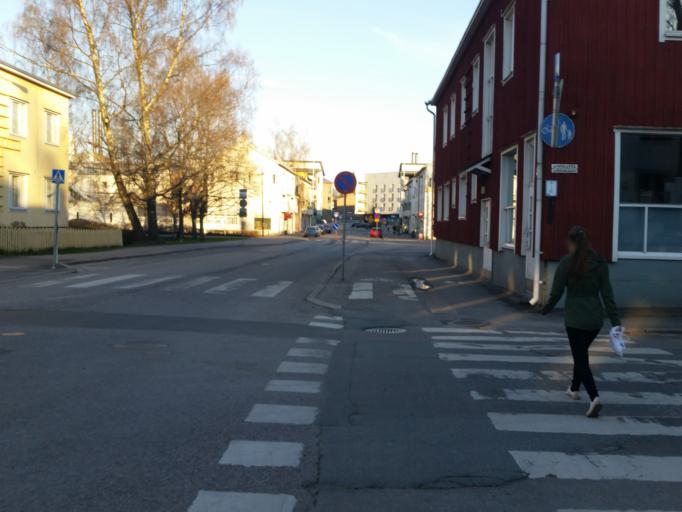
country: FI
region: Uusimaa
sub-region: Helsinki
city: Helsinki
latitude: 60.2094
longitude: 24.9644
